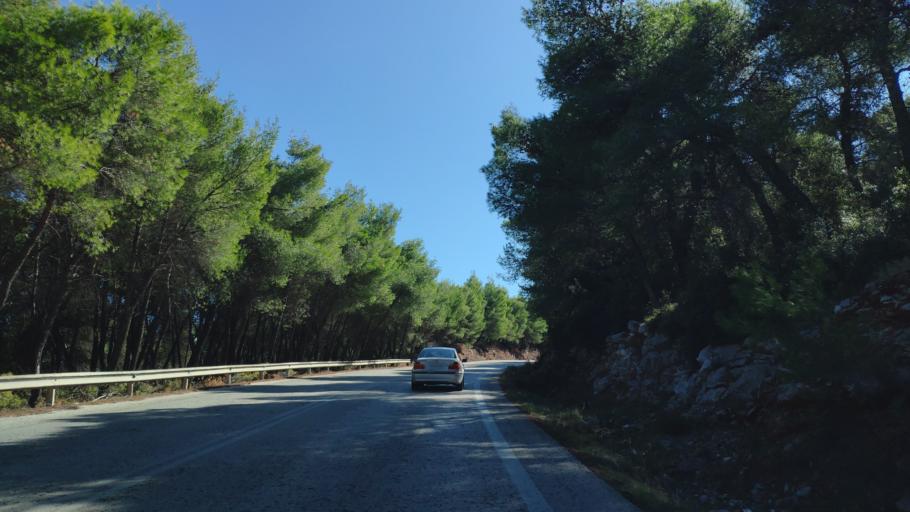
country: GR
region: Peloponnese
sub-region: Nomos Korinthias
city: Sofikon
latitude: 37.8257
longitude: 23.1019
